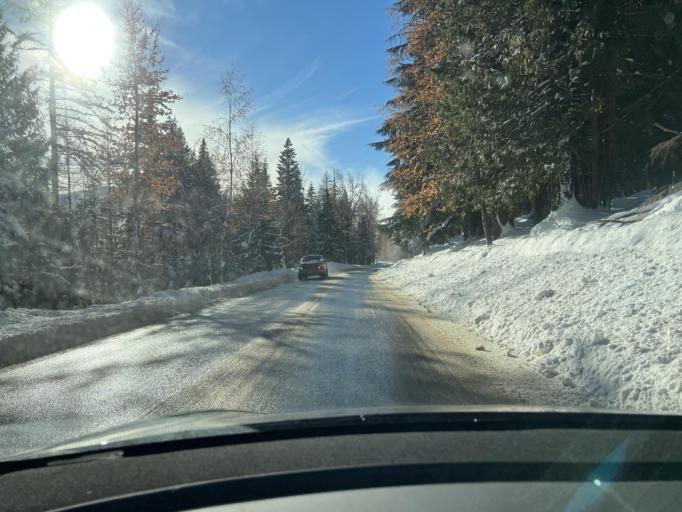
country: US
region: Idaho
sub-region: Bonner County
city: Ponderay
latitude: 48.3430
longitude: -116.6001
